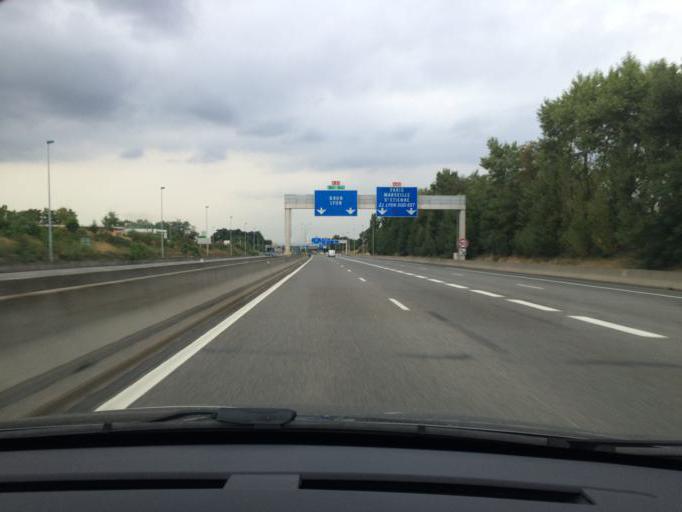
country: FR
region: Rhone-Alpes
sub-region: Departement du Rhone
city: Saint-Priest
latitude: 45.6975
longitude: 4.9774
